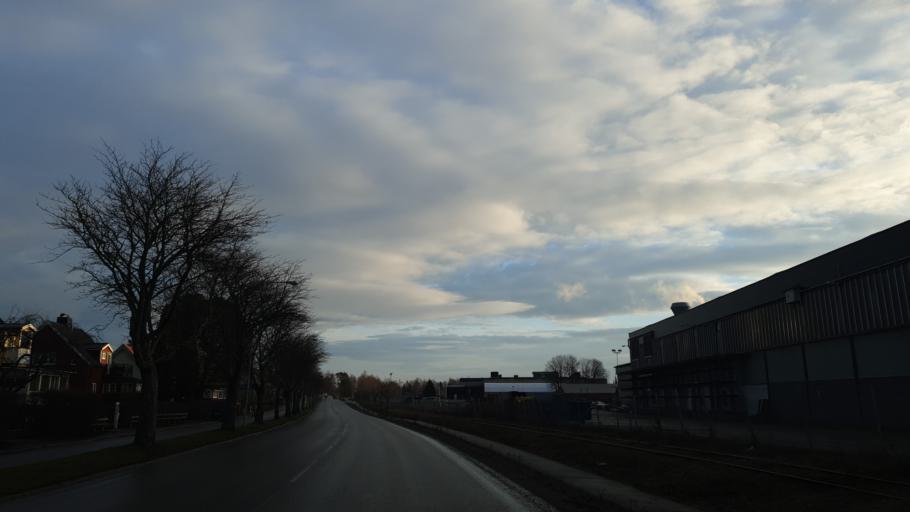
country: SE
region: Gaevleborg
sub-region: Hudiksvalls Kommun
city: Hudiksvall
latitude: 61.7248
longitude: 17.1316
